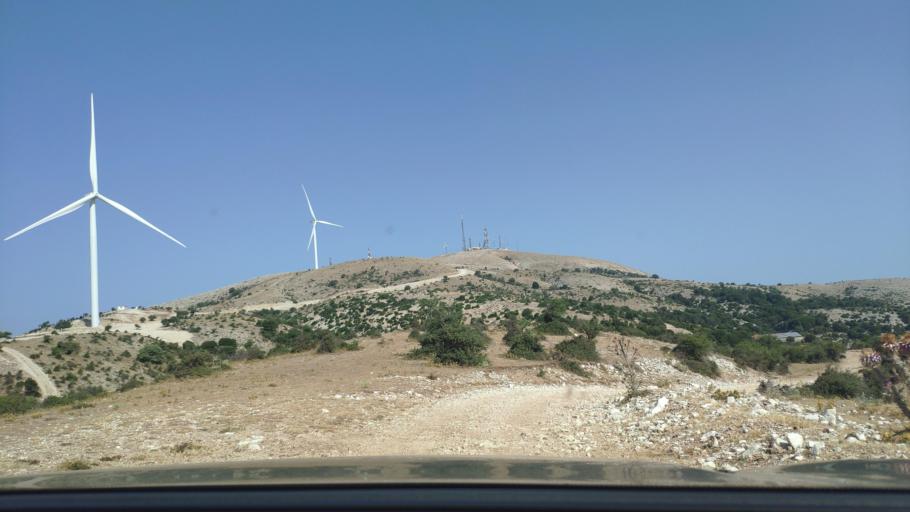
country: GR
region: West Greece
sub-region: Nomos Aitolias kai Akarnanias
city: Monastirakion
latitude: 38.7971
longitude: 20.9983
